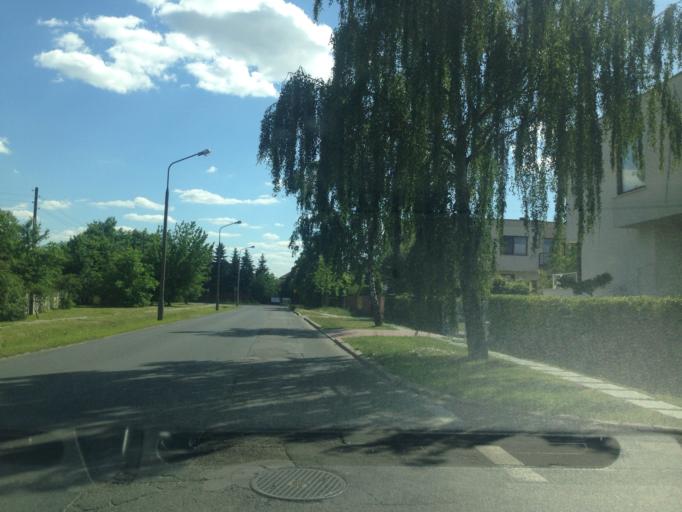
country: PL
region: Masovian Voivodeship
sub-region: Warszawa
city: Bemowo
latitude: 52.2492
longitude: 20.8802
